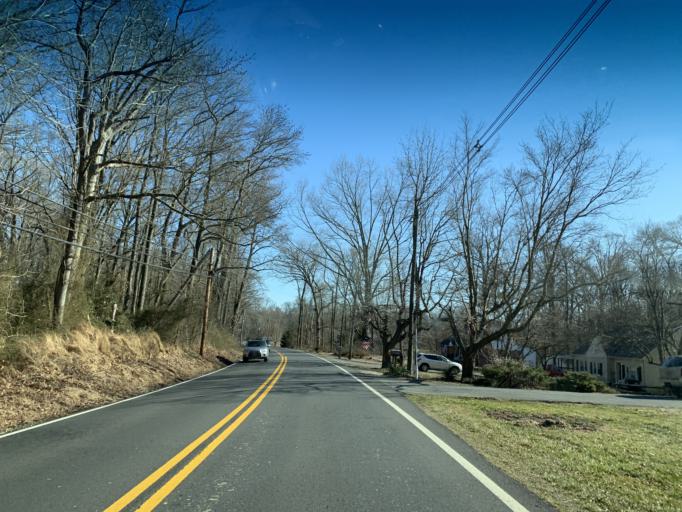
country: US
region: Maryland
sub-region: Cecil County
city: Elkton
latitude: 39.6355
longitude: -75.8636
